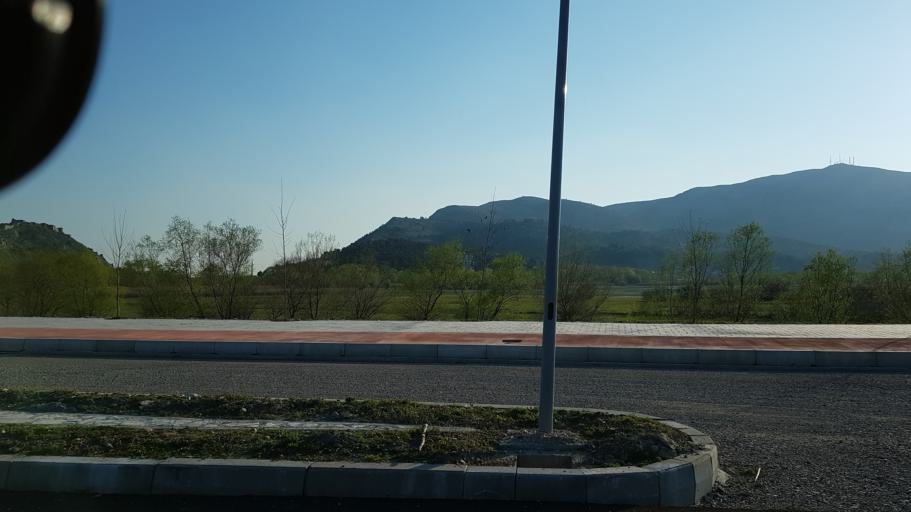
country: AL
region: Shkoder
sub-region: Rrethi i Shkodres
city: Shkoder
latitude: 42.0610
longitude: 19.4955
